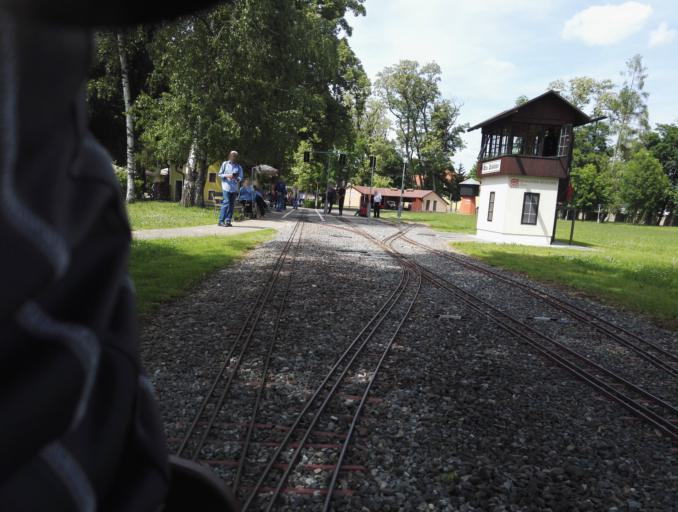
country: AT
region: Styria
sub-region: Graz Stadt
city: Wetzelsdorf
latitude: 47.0400
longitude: 15.4150
